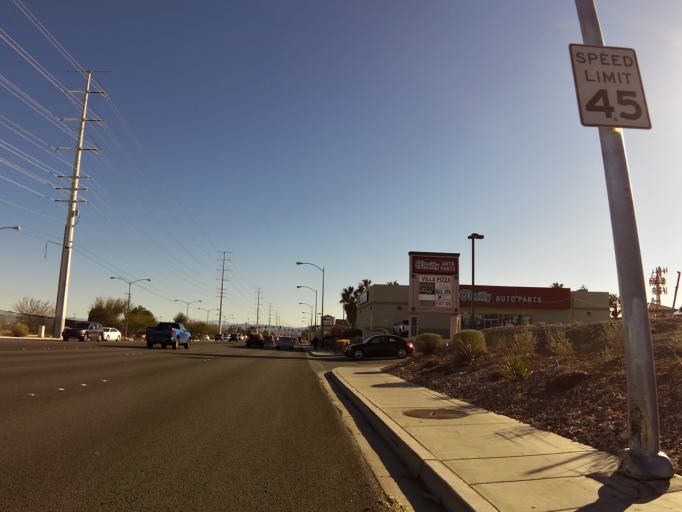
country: US
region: Nevada
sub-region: Clark County
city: Spring Valley
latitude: 36.1285
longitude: -115.2792
